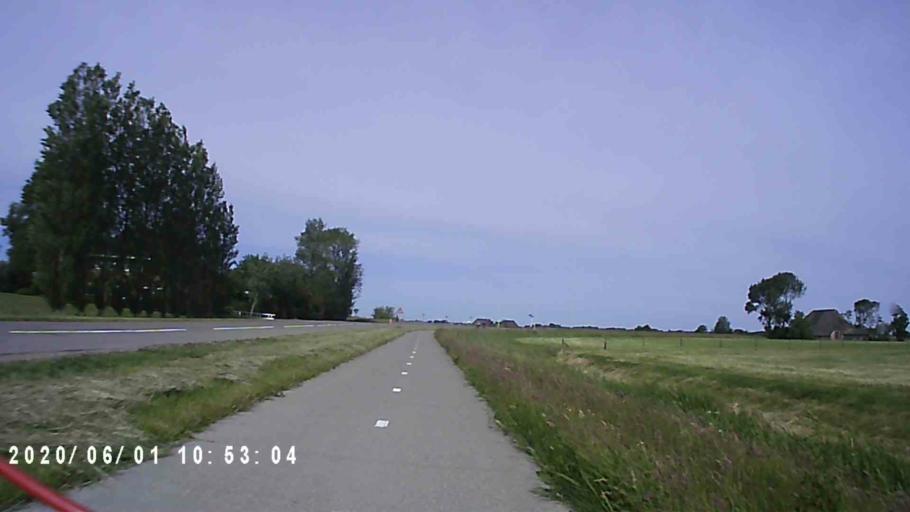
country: NL
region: Friesland
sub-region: Gemeente Franekeradeel
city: Franeker
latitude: 53.2012
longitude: 5.5150
